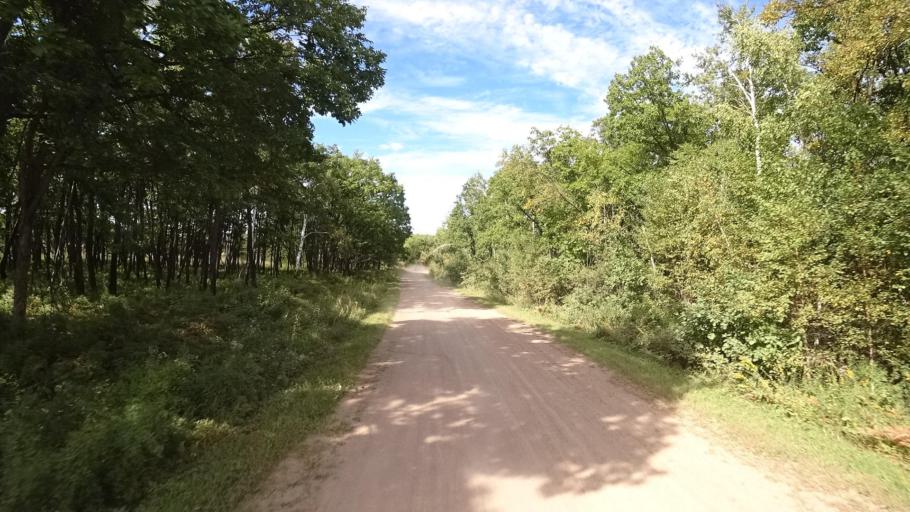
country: RU
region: Primorskiy
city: Yakovlevka
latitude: 44.3817
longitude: 133.5357
